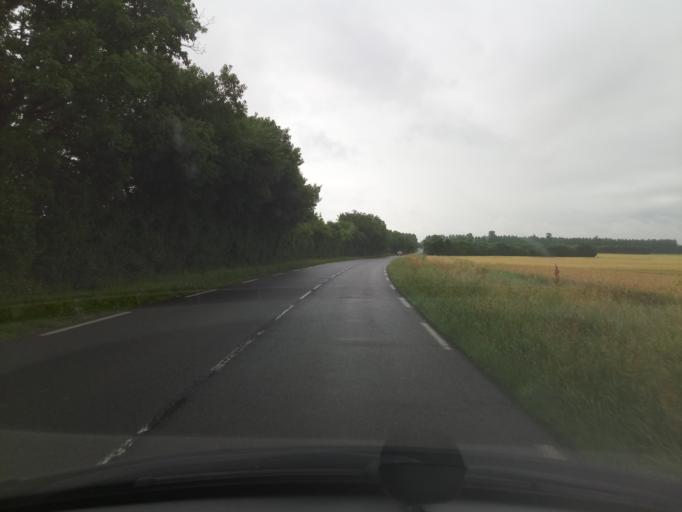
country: FR
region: Poitou-Charentes
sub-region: Departement de la Charente-Maritime
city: Courcon
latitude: 46.1741
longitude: -0.8425
